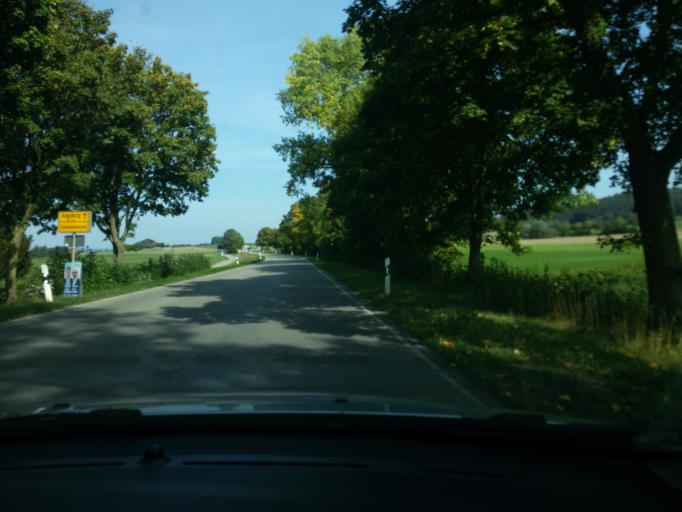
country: DE
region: Bavaria
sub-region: Swabia
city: Ziemetshausen
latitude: 48.2924
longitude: 10.5420
